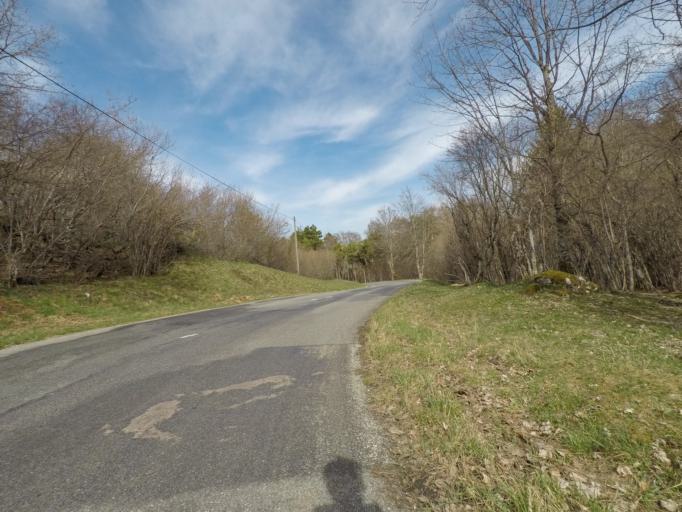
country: CH
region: Geneva
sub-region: Geneva
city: Veyrier
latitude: 46.1474
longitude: 6.1887
